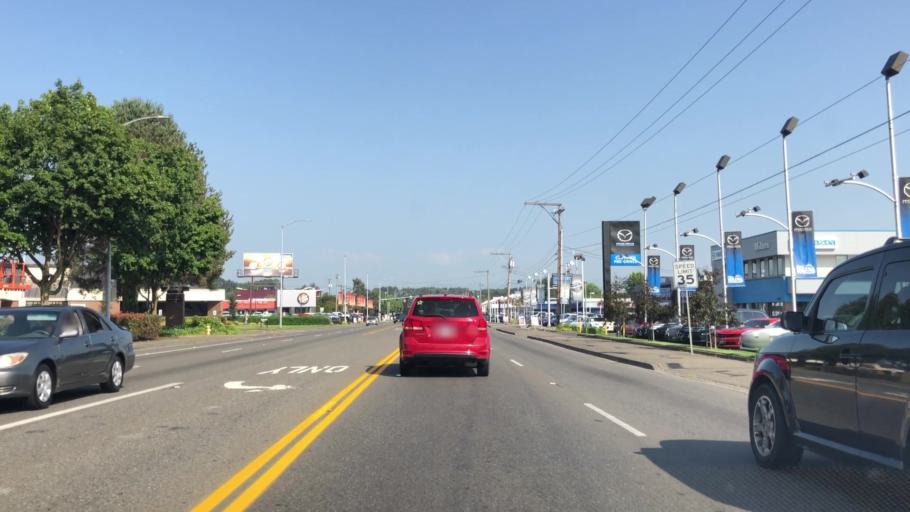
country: US
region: Washington
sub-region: Pierce County
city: Puyallup
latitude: 47.2007
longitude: -122.3016
